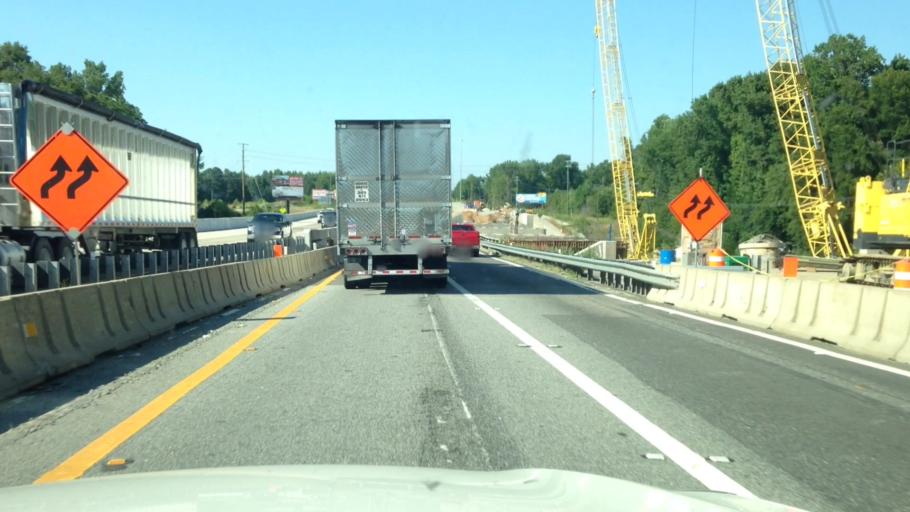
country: US
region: Virginia
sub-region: City of Emporia
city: Emporia
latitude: 36.6942
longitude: -77.5544
